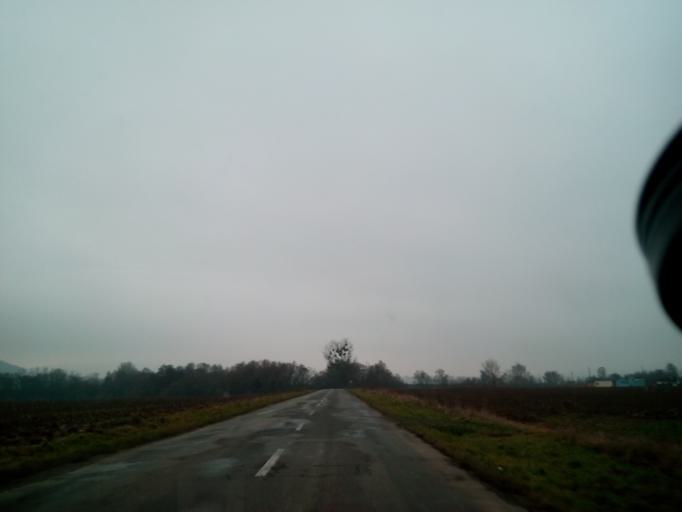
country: SK
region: Kosicky
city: Kosice
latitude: 48.7243
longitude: 21.4377
